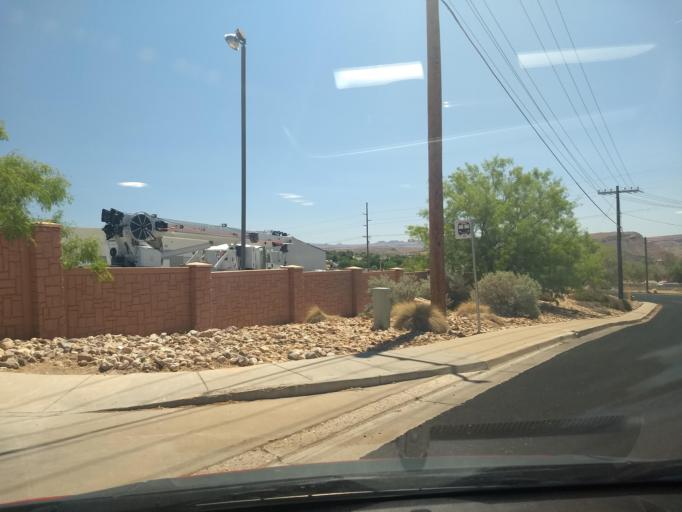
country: US
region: Utah
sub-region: Washington County
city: Washington
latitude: 37.1332
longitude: -113.5214
